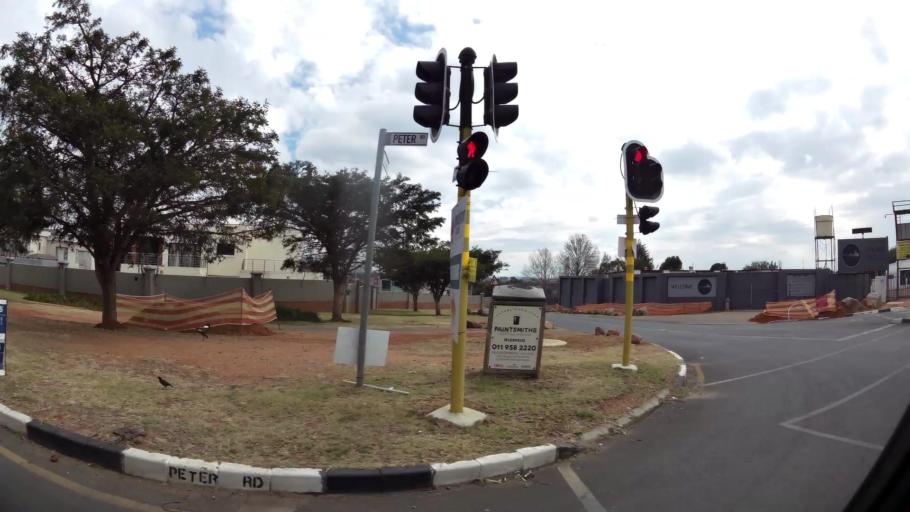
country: ZA
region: Gauteng
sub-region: West Rand District Municipality
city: Muldersdriseloop
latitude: -26.0850
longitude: 27.8734
